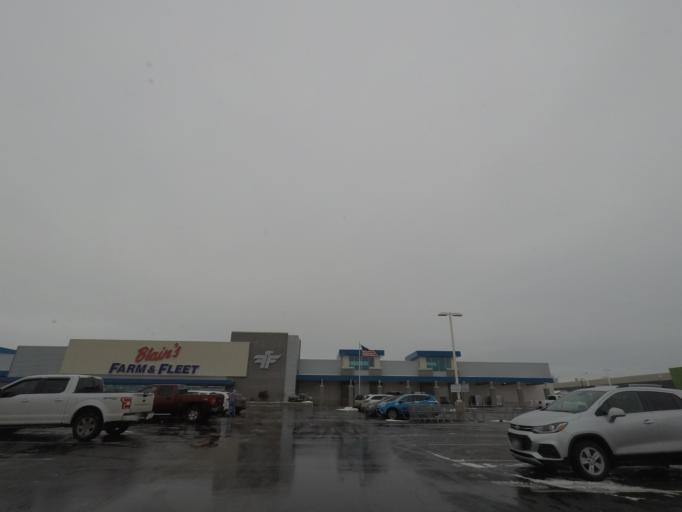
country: US
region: Wisconsin
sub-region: Dane County
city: Verona
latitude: 42.9949
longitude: -89.5214
